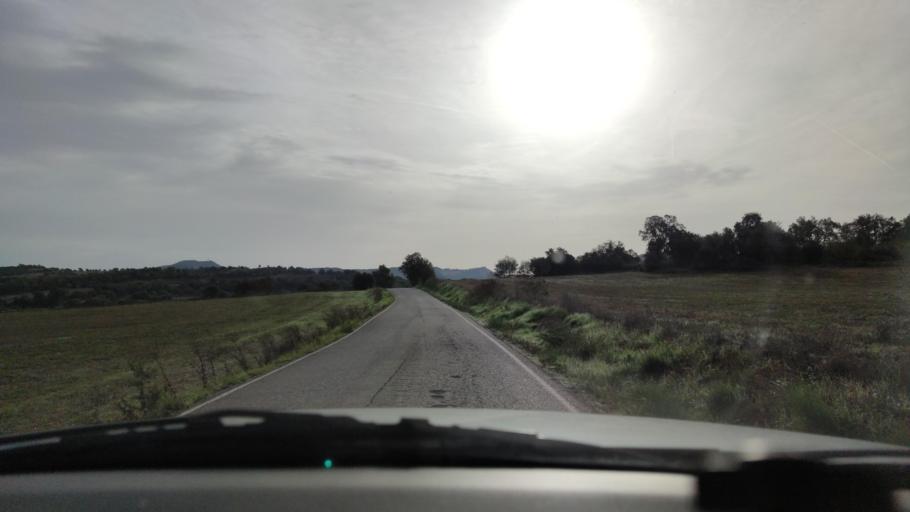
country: ES
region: Catalonia
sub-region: Provincia de Lleida
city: Artesa de Segre
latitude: 41.9082
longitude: 1.0361
